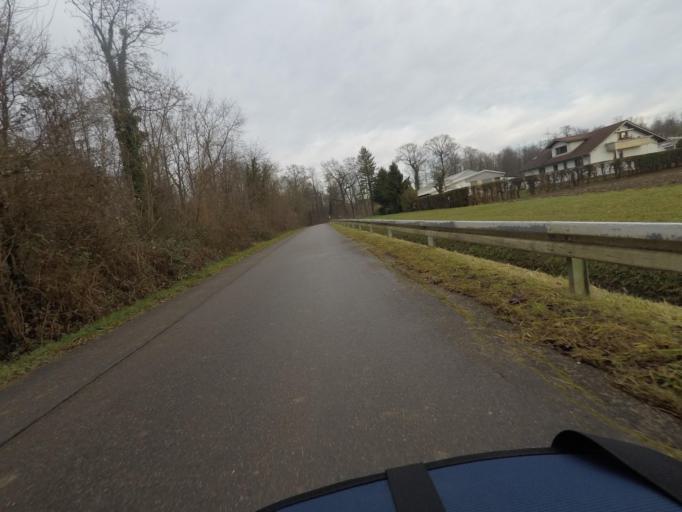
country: DE
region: Baden-Wuerttemberg
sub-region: Karlsruhe Region
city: Rheinau
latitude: 48.8675
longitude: 8.1645
